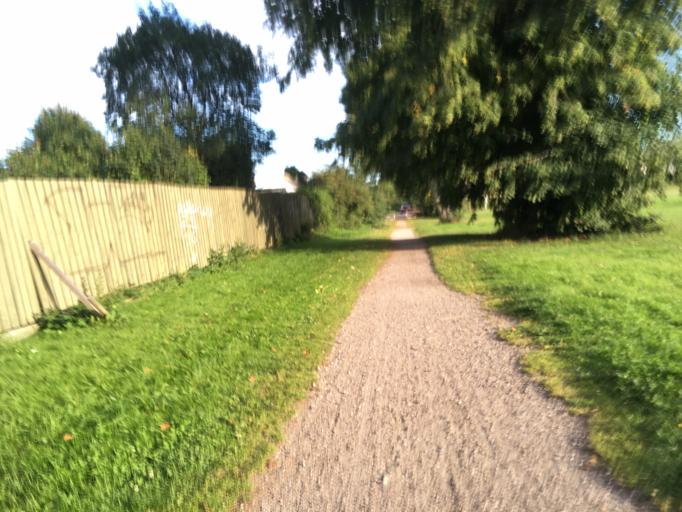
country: DK
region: Capital Region
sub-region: Hillerod Kommune
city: Hillerod
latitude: 55.9260
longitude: 12.2978
